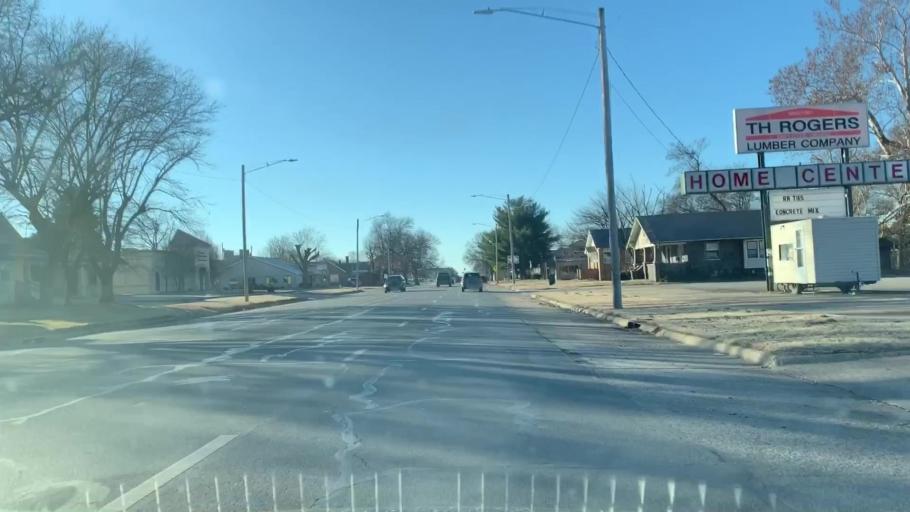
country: US
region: Kansas
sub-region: Crawford County
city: Pittsburg
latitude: 37.4232
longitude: -94.7050
